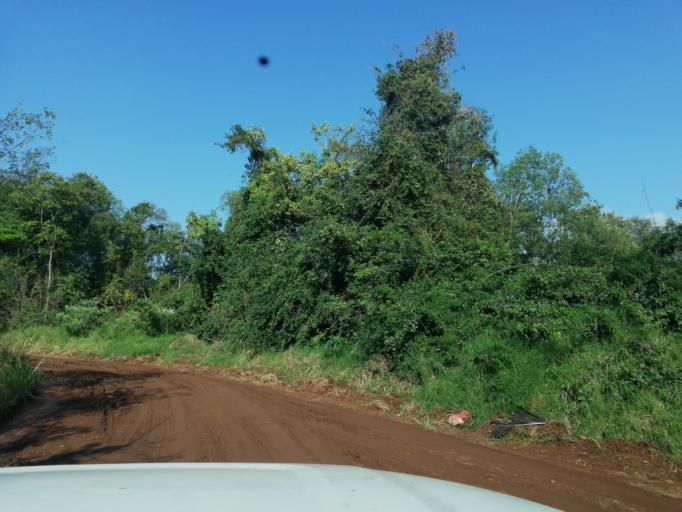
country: AR
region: Misiones
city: Cerro Azul
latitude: -27.6208
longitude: -55.5277
